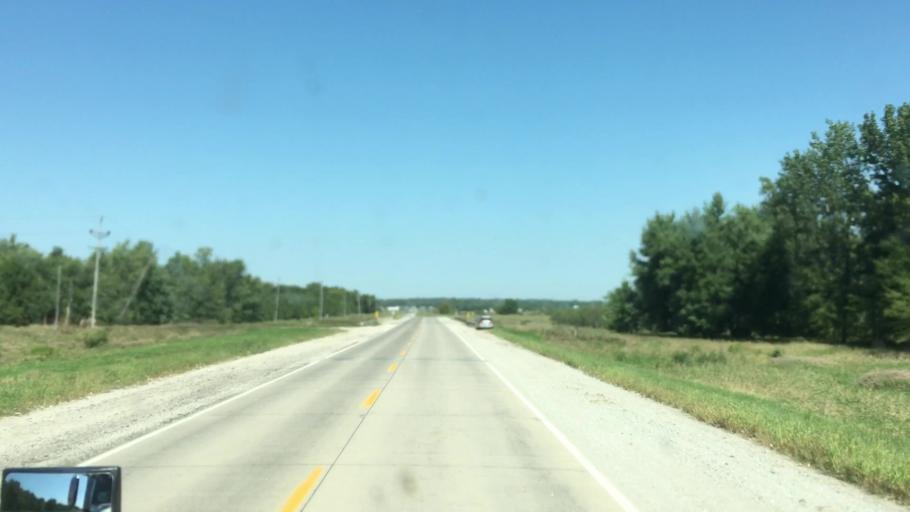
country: US
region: Iowa
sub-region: Benton County
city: Belle Plaine
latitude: 41.8657
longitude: -92.2778
